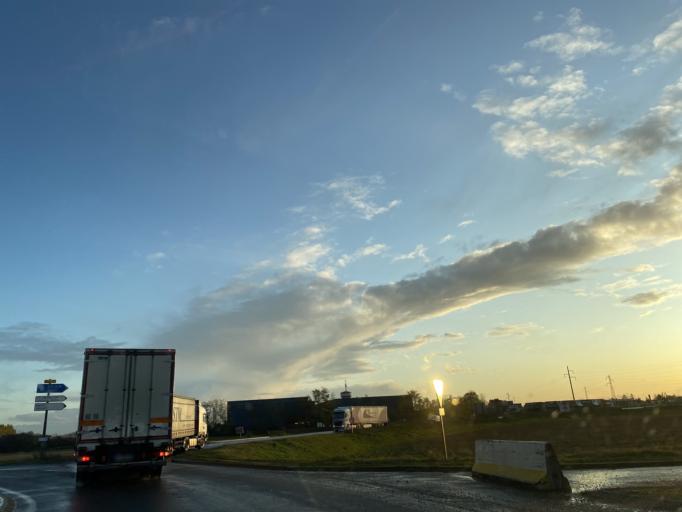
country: FR
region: Centre
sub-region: Departement du Loiret
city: Artenay
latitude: 48.0851
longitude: 1.8682
